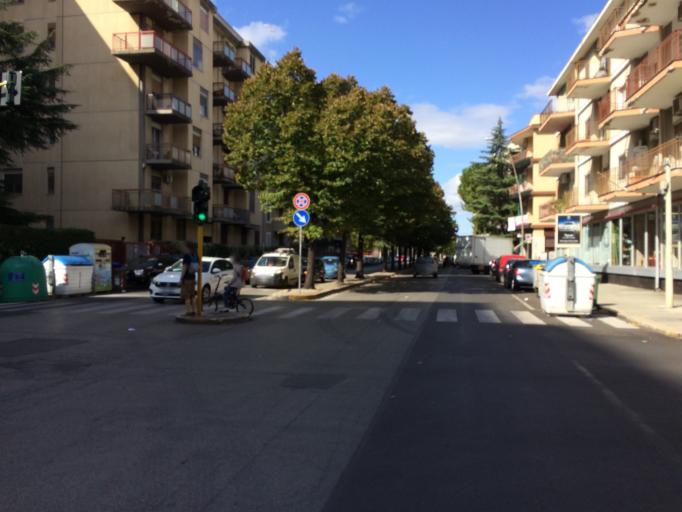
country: IT
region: Apulia
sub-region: Provincia di Bari
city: Bari
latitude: 41.1011
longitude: 16.8649
